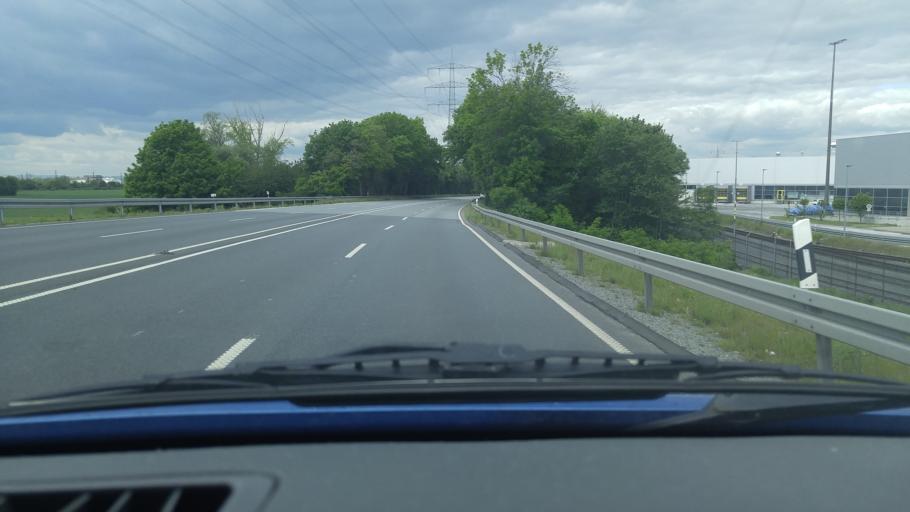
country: DE
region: Hesse
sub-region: Regierungsbezirk Darmstadt
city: Bischofsheim
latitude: 49.9853
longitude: 8.3845
